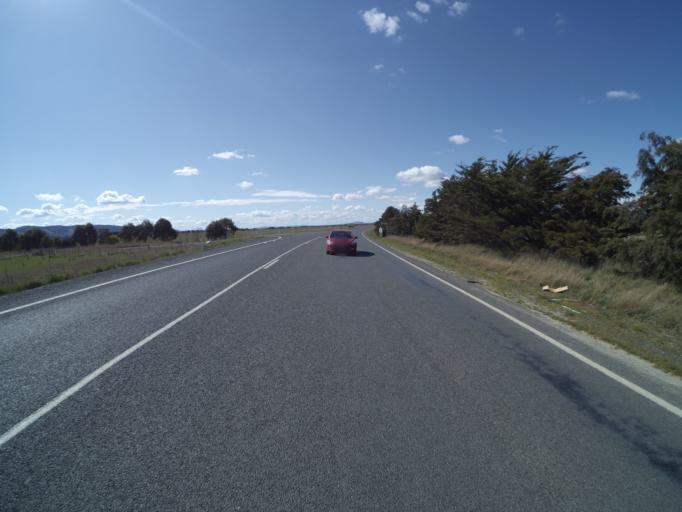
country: AU
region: New South Wales
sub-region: Palerang
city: Bungendore
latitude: -35.2793
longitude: 149.4227
